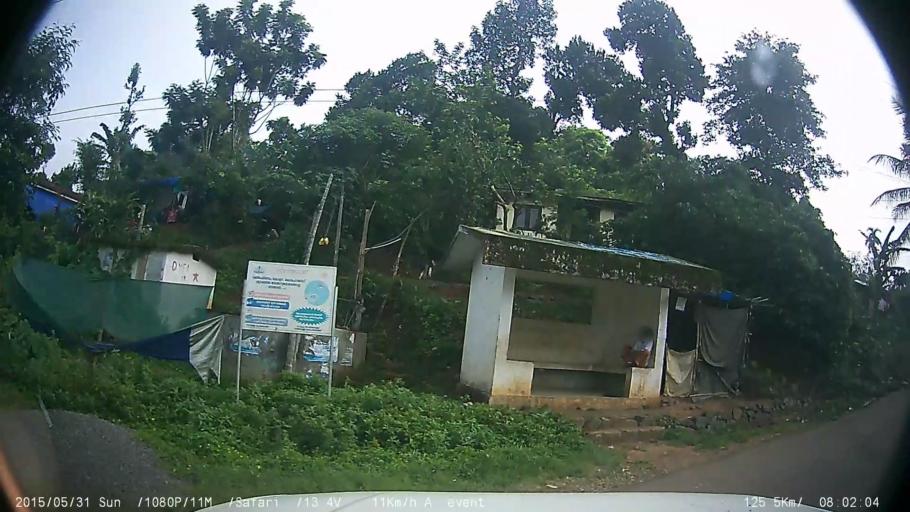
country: IN
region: Kerala
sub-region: Wayanad
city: Kalpetta
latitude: 11.6339
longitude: 76.0444
